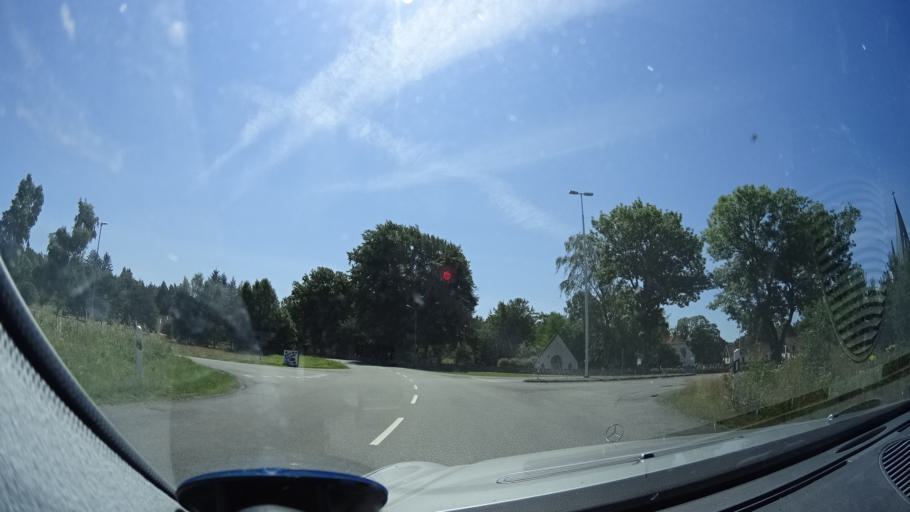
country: SE
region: Skane
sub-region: Kristianstads Kommun
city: Onnestad
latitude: 55.9283
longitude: 13.9684
